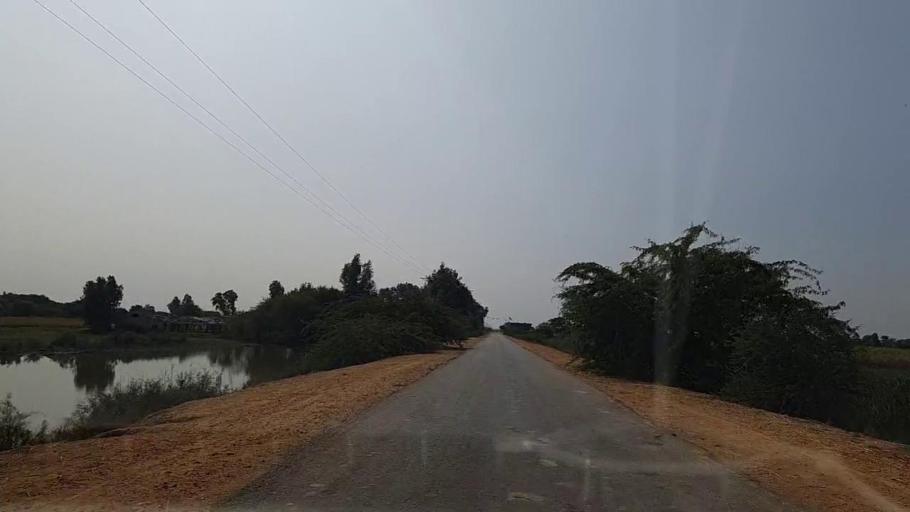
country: PK
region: Sindh
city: Chuhar Jamali
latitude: 24.3600
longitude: 67.9596
